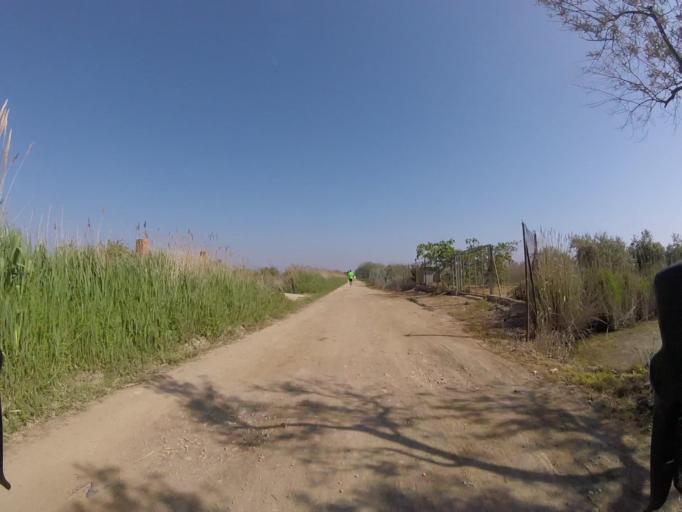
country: ES
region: Valencia
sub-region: Provincia de Castello
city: Orpesa/Oropesa del Mar
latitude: 40.1433
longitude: 0.1642
